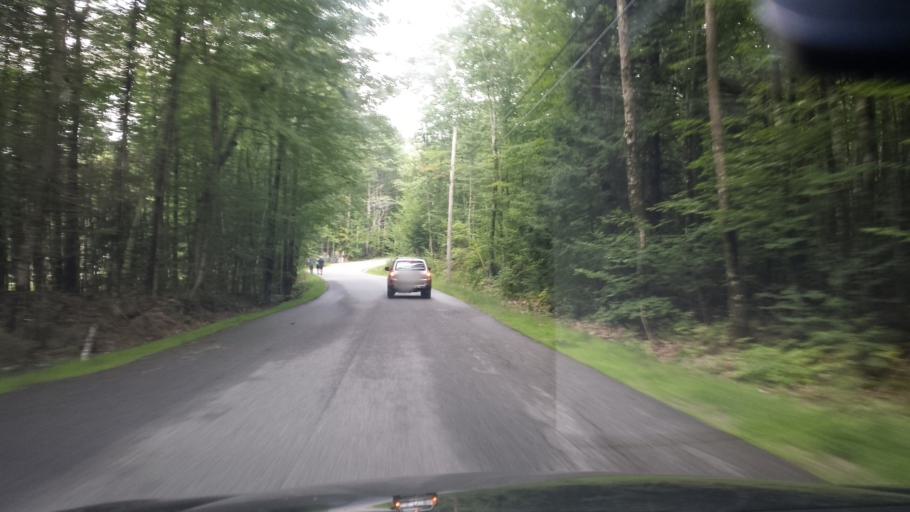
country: US
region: Maine
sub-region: York County
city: Alfred
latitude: 43.4991
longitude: -70.6428
